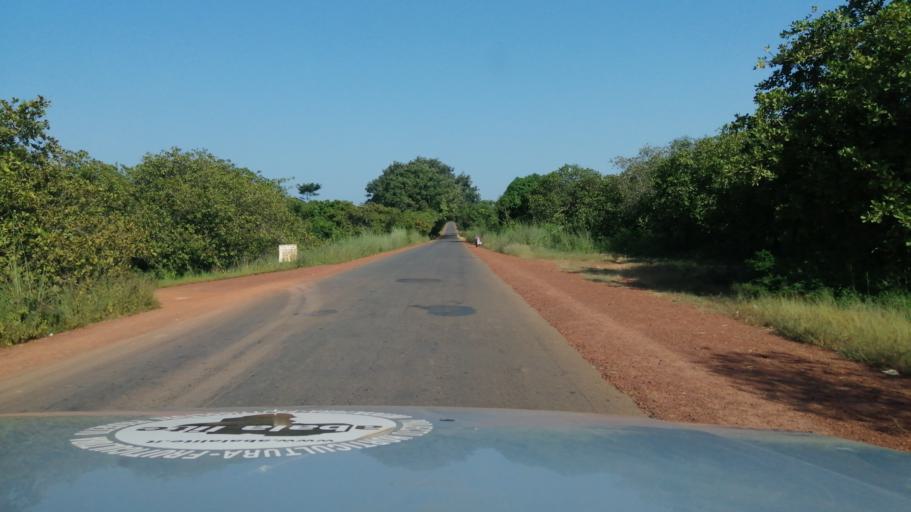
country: GW
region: Bissau
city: Bissau
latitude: 11.9589
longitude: -15.5309
